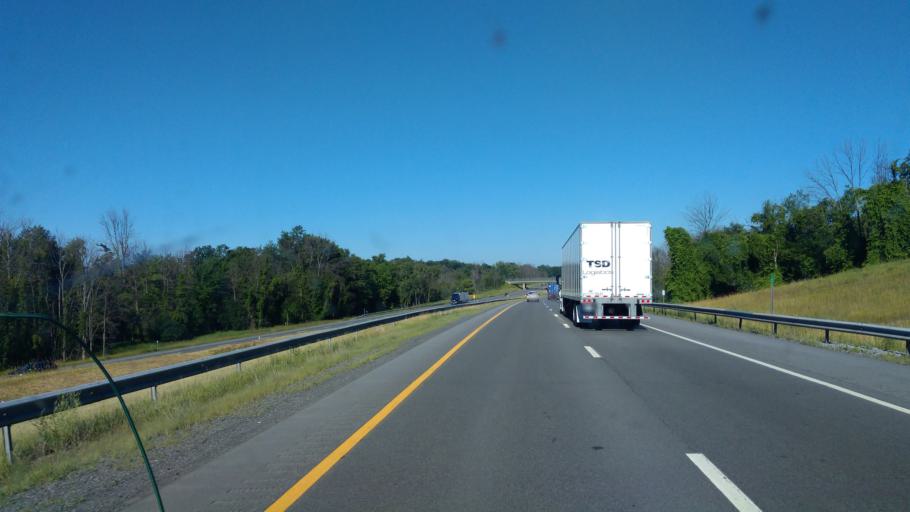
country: US
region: New York
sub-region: Livingston County
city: Caledonia
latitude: 43.0301
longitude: -77.8371
